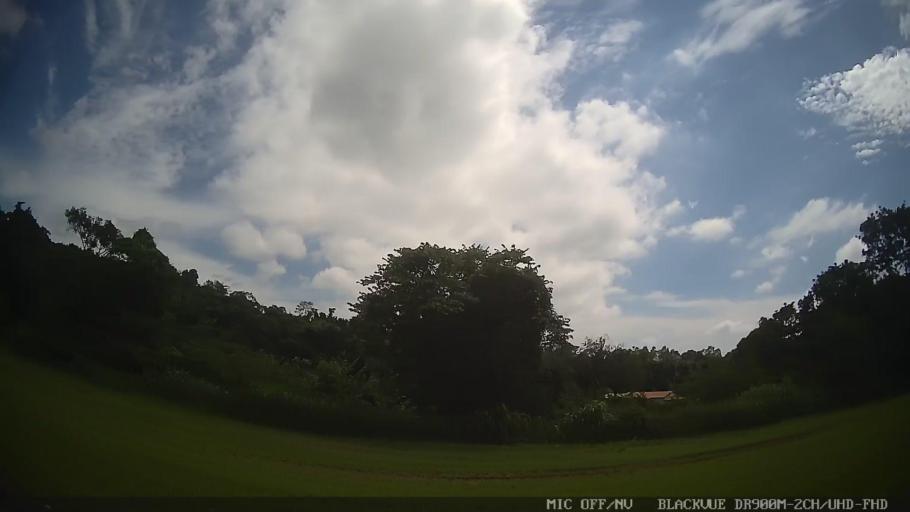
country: BR
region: Sao Paulo
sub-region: Tiete
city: Tiete
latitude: -23.1074
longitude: -47.7590
